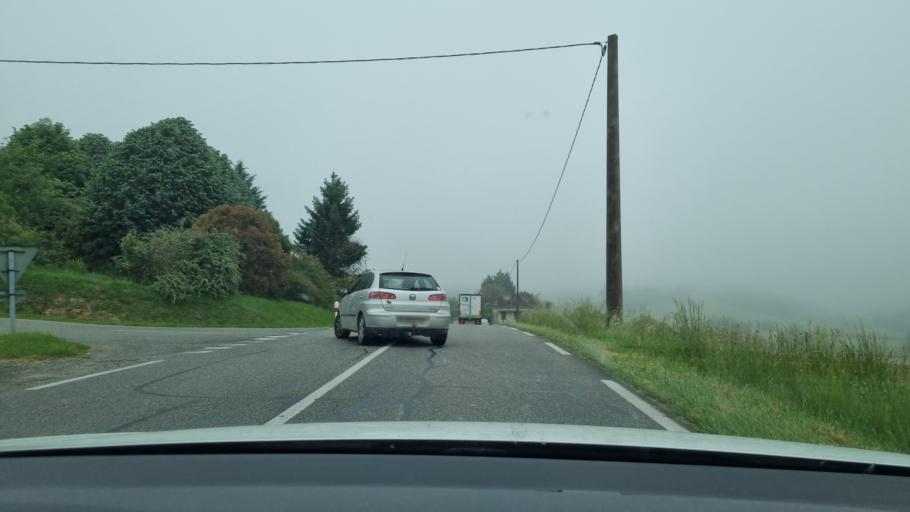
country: FR
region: Aquitaine
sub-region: Departement des Pyrenees-Atlantiques
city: Orthez
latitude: 43.5104
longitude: -0.7297
